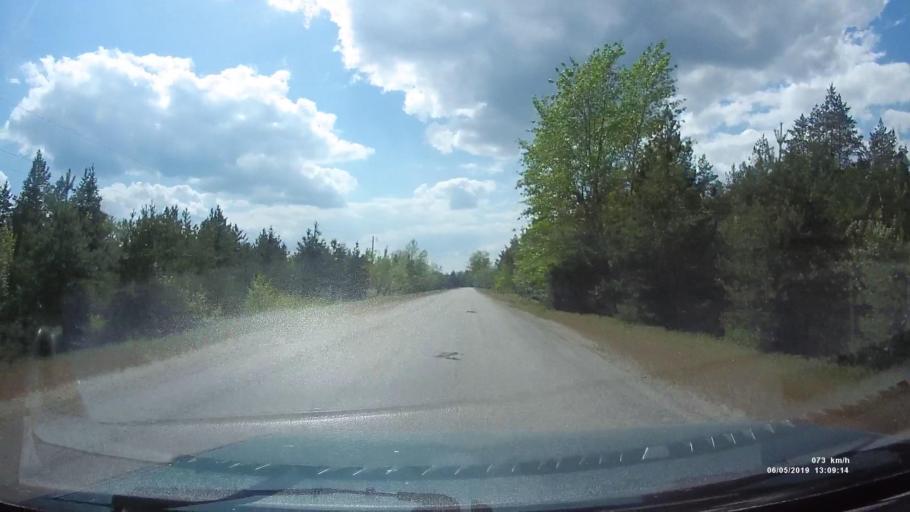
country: RU
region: Rostov
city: Ust'-Donetskiy
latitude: 47.7700
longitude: 40.9866
